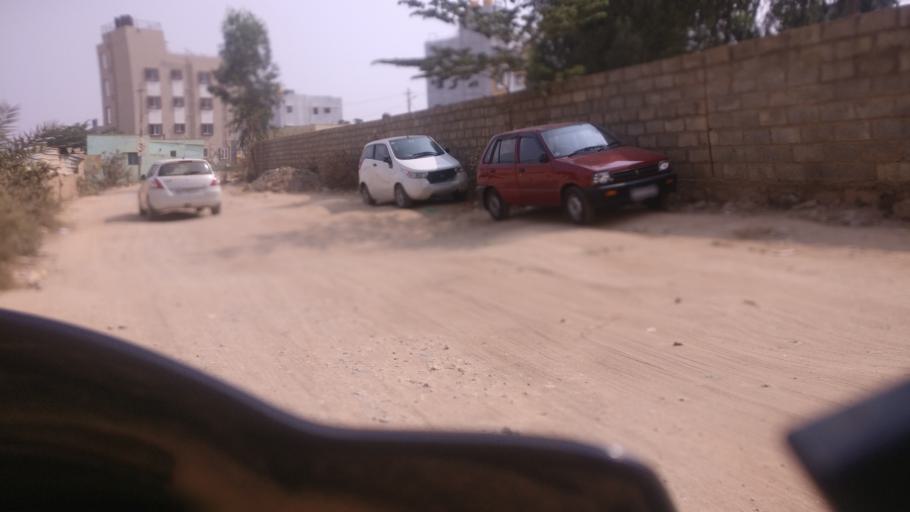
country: IN
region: Karnataka
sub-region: Bangalore Urban
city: Bangalore
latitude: 12.8961
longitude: 77.6787
